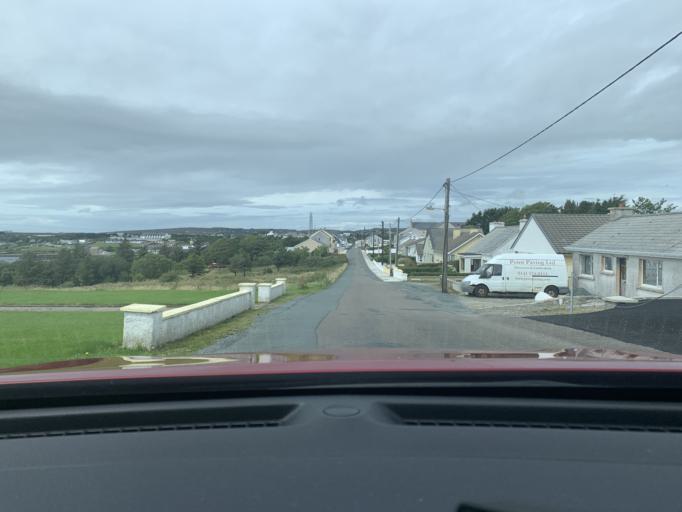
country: IE
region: Ulster
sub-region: County Donegal
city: Dungloe
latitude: 54.9454
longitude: -8.3588
